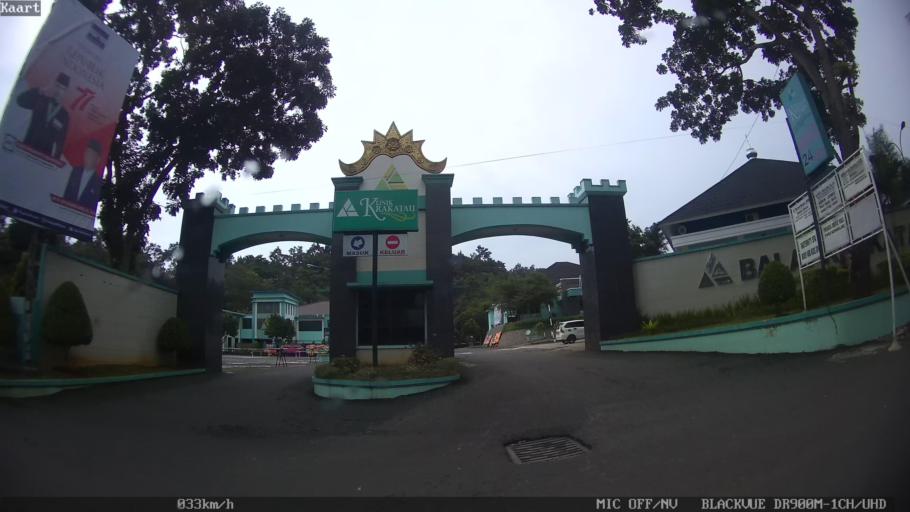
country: ID
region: Lampung
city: Kedaton
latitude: -5.3939
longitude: 105.2220
